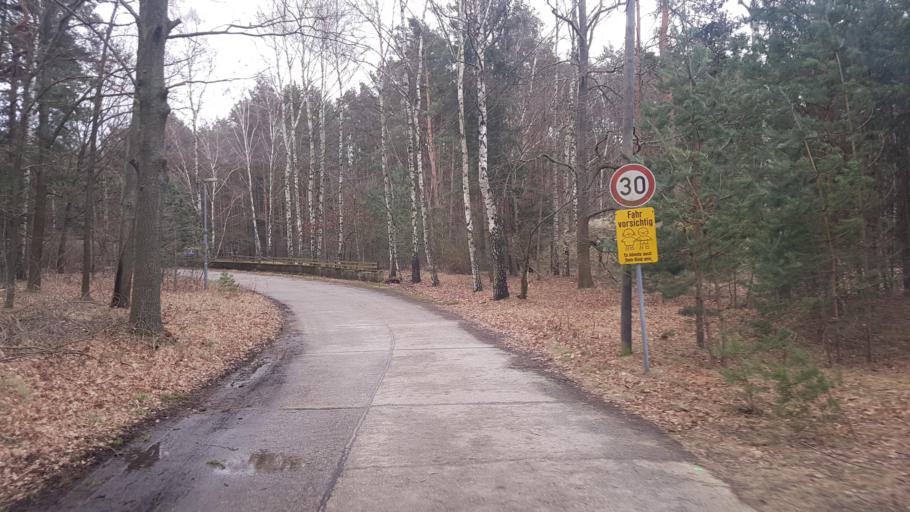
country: DE
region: Brandenburg
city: Kroppen
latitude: 51.3776
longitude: 13.8081
